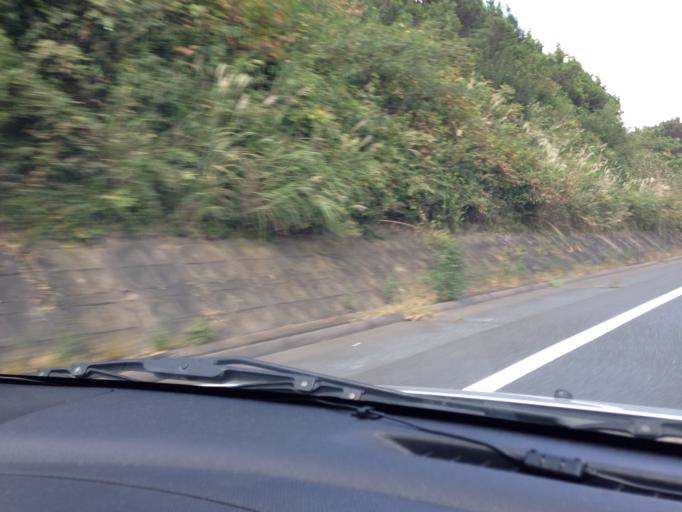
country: JP
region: Ibaraki
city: Mito-shi
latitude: 36.4012
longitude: 140.3920
